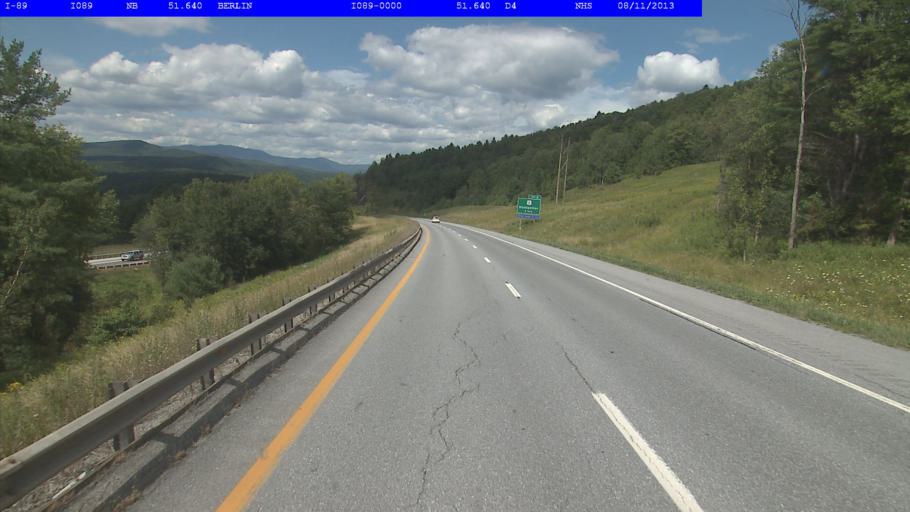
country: US
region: Vermont
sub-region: Washington County
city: Montpelier
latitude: 44.2351
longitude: -72.5847
